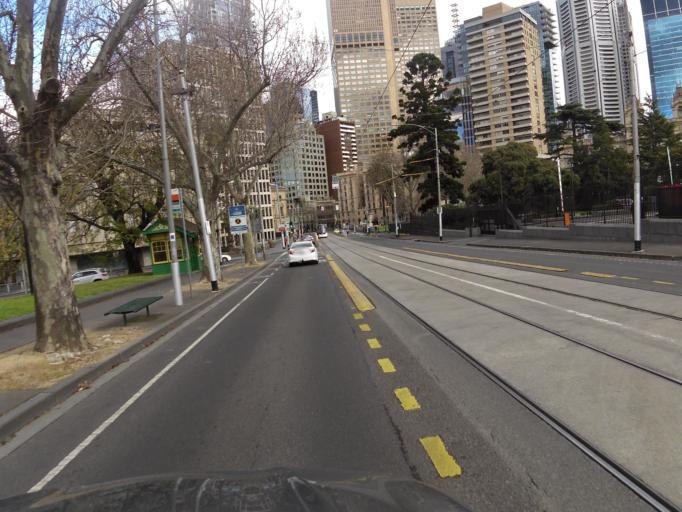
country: AU
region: Victoria
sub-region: Melbourne
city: Melbourne
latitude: -37.8113
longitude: 144.9750
